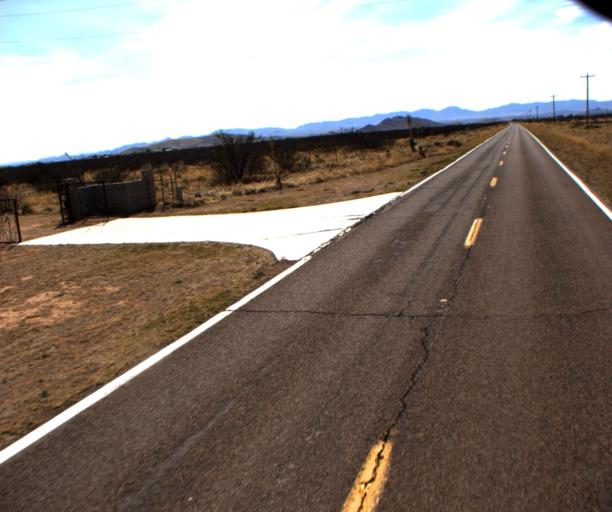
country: US
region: Arizona
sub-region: Cochise County
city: Willcox
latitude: 31.8761
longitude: -109.5869
